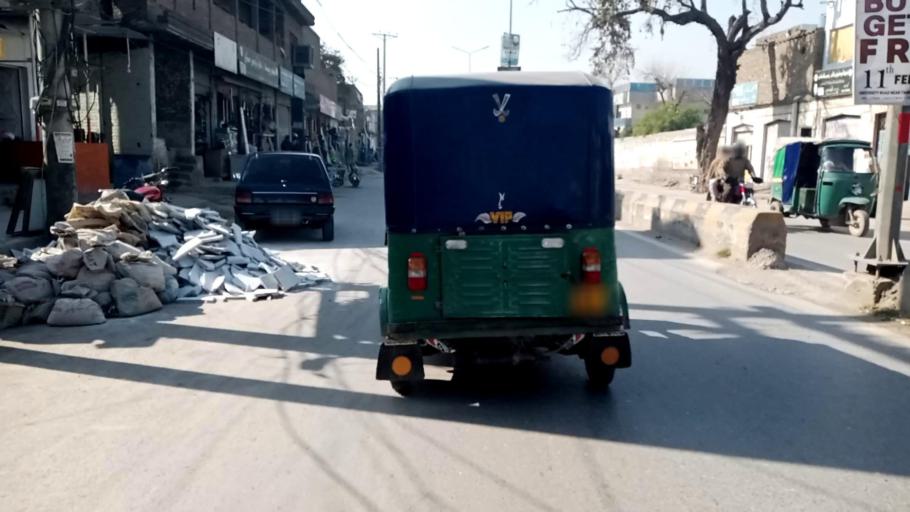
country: PK
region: Khyber Pakhtunkhwa
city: Peshawar
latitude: 33.9794
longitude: 71.5222
